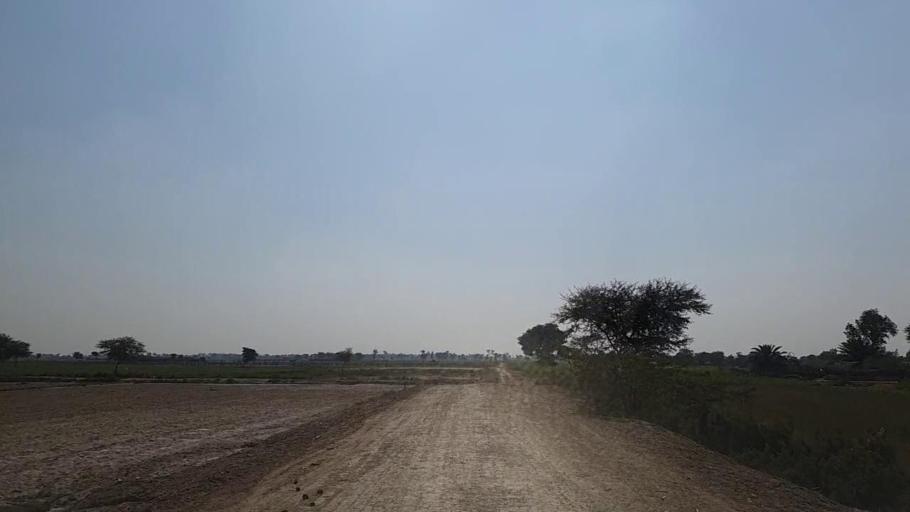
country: PK
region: Sindh
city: Daur
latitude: 26.4548
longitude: 68.2708
